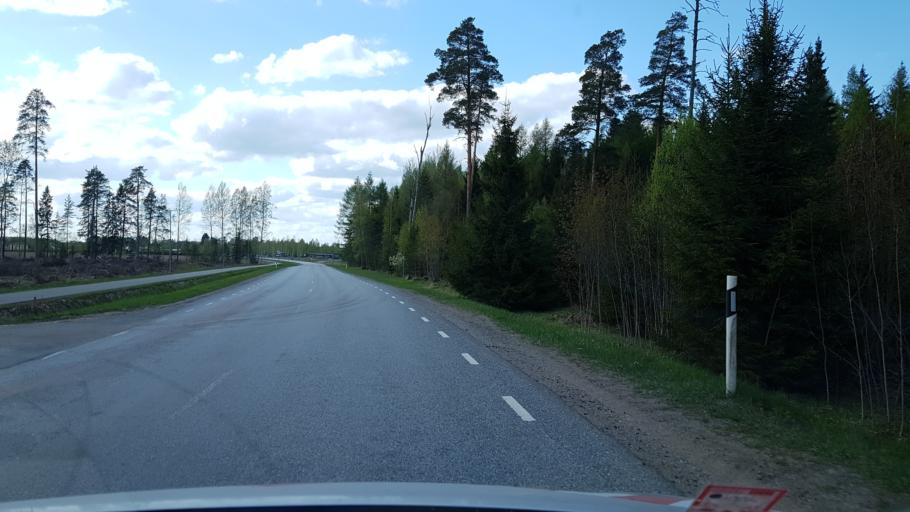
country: EE
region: Tartu
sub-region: UElenurme vald
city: Ulenurme
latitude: 58.3185
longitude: 26.8338
